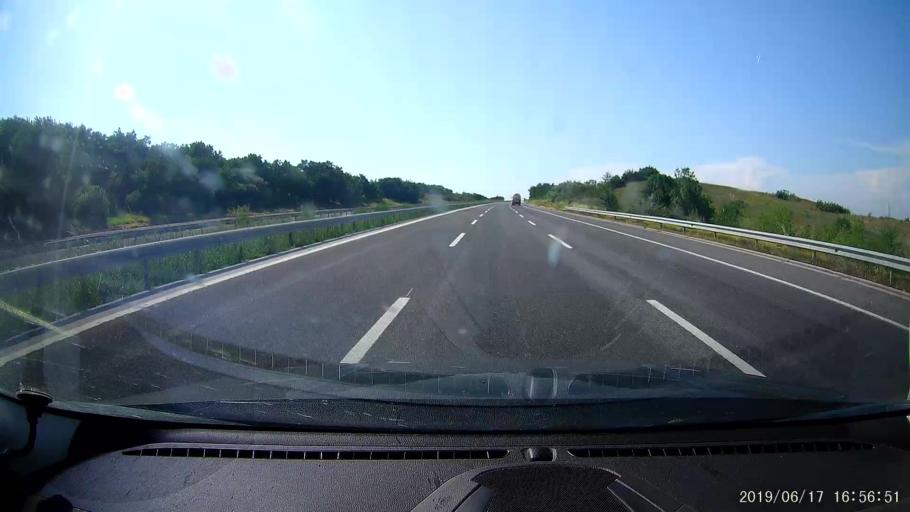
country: TR
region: Edirne
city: Haskoy
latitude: 41.5916
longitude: 26.9270
